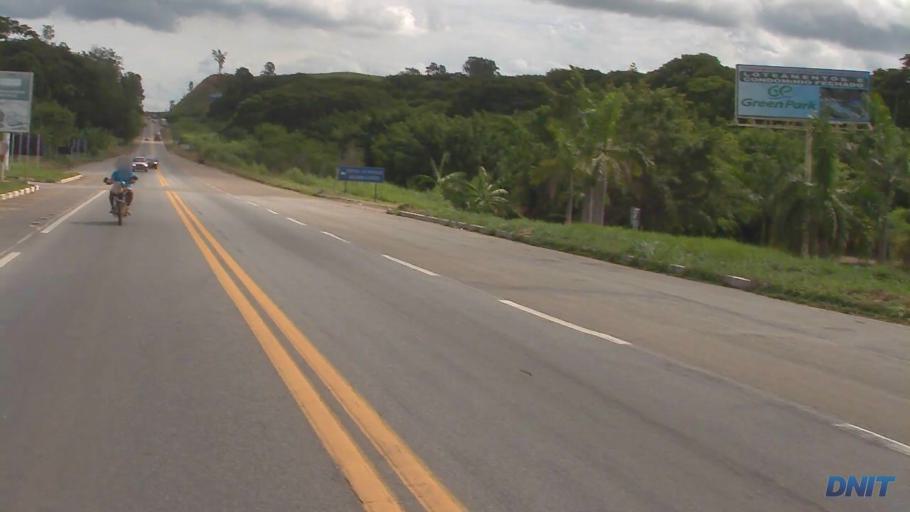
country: BR
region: Minas Gerais
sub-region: Ipatinga
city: Ipatinga
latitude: -19.4400
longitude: -42.5115
